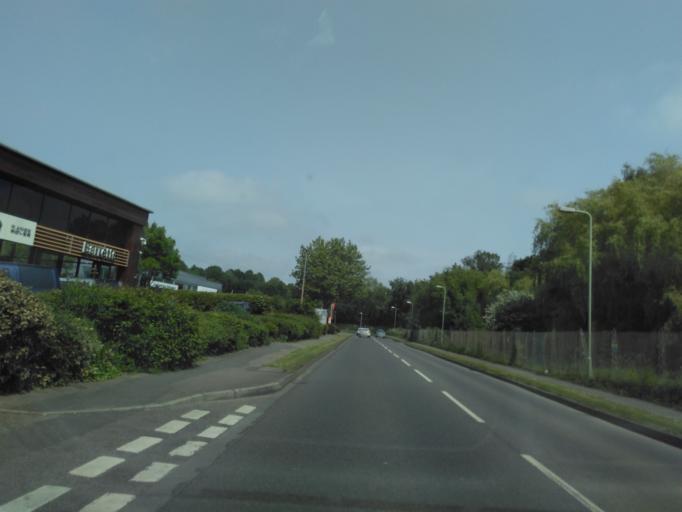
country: GB
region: England
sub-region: Kent
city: Canterbury
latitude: 51.2937
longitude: 1.0936
